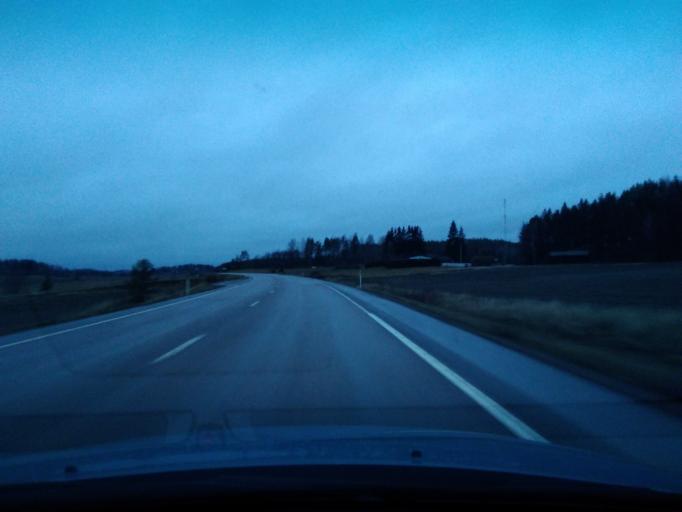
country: FI
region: Uusimaa
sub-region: Porvoo
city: Askola
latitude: 60.4746
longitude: 25.5688
